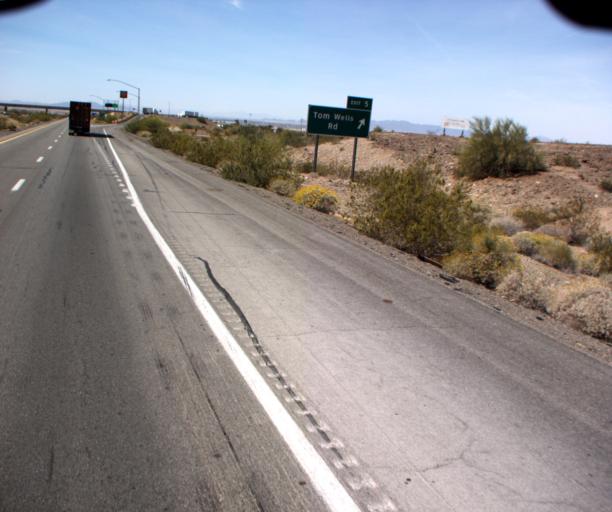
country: US
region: Arizona
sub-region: La Paz County
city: Ehrenberg
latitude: 33.6257
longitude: -114.4298
